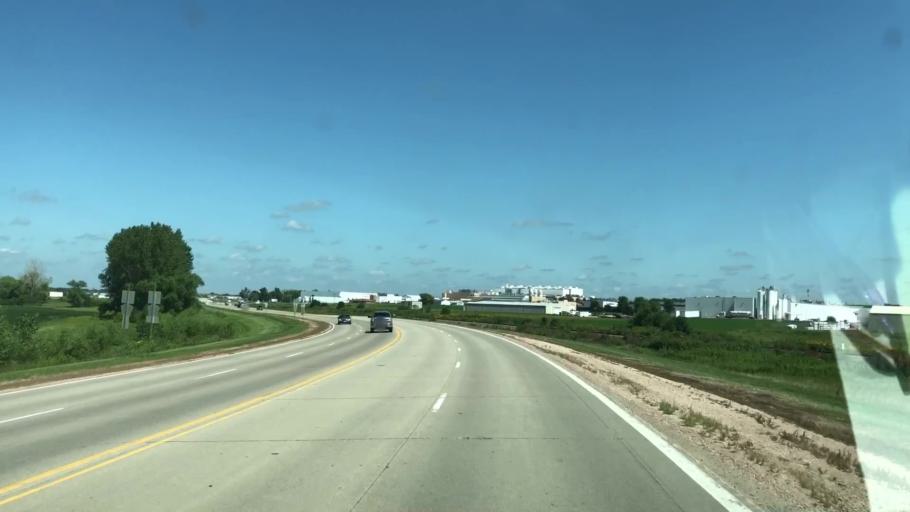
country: US
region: Iowa
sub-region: Plymouth County
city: Le Mars
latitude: 42.7648
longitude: -96.2000
